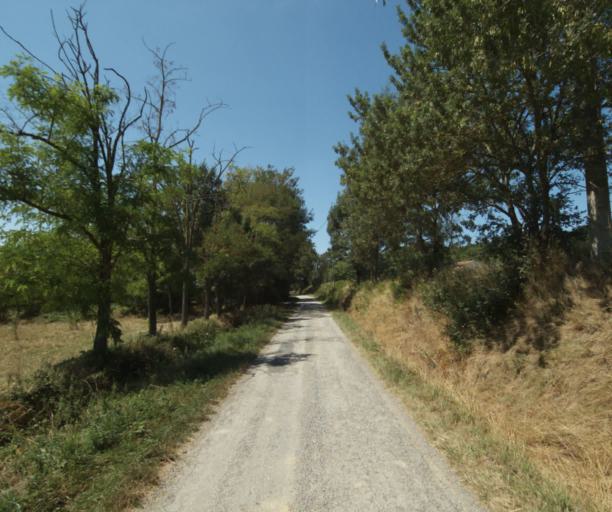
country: FR
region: Midi-Pyrenees
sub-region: Departement de la Haute-Garonne
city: Auriac-sur-Vendinelle
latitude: 43.5017
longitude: 1.8610
